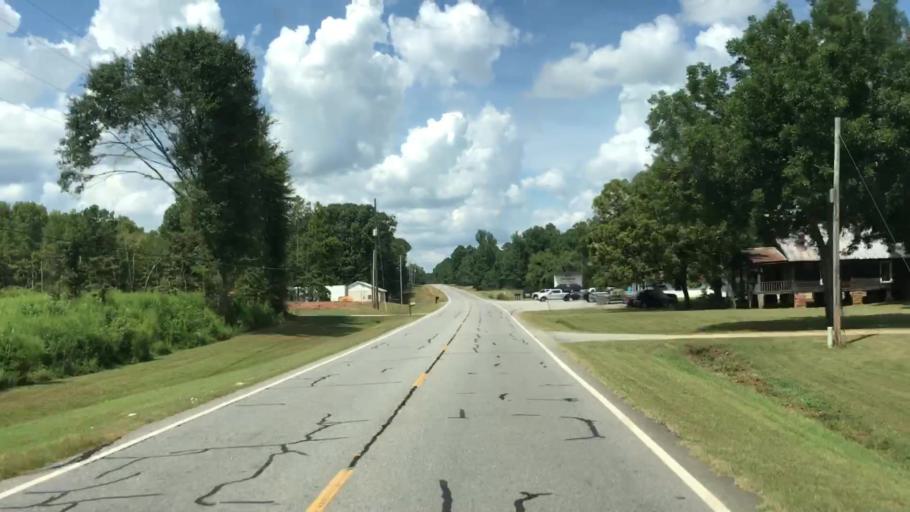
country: US
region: Georgia
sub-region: Oconee County
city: Watkinsville
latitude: 33.8056
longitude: -83.3454
